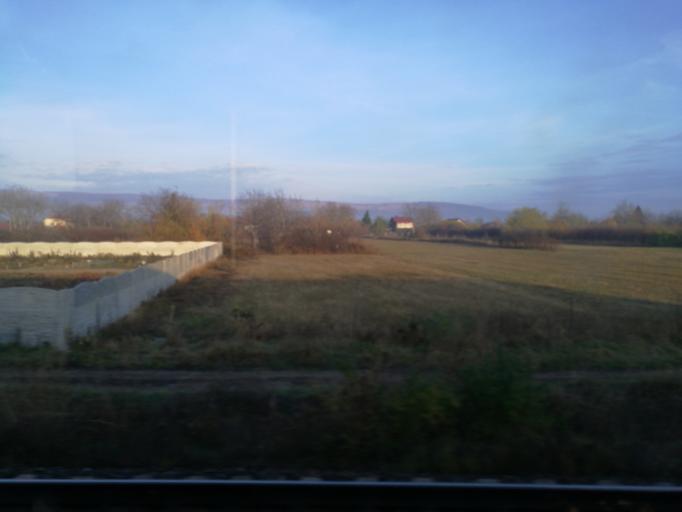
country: RO
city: Valcele
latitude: 45.0784
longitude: 26.6441
